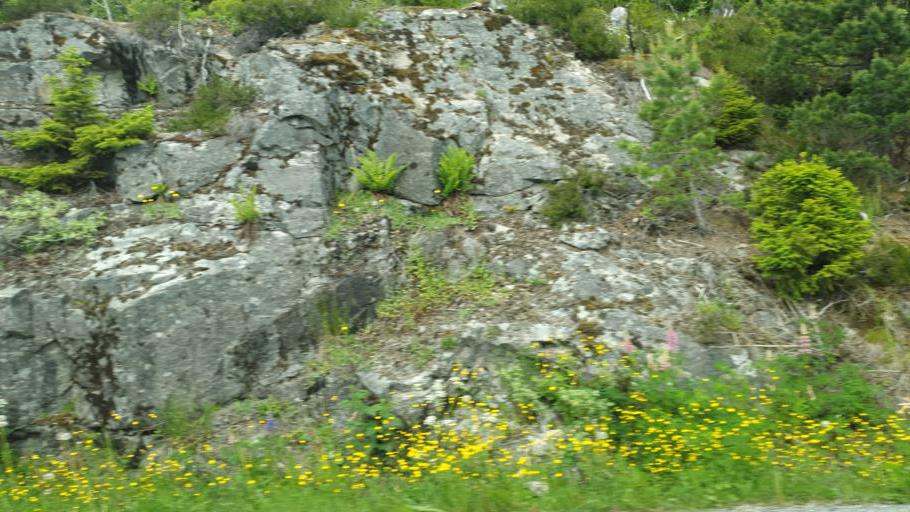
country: NO
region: Sor-Trondelag
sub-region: Trondheim
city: Trondheim
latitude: 63.5712
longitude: 10.3467
